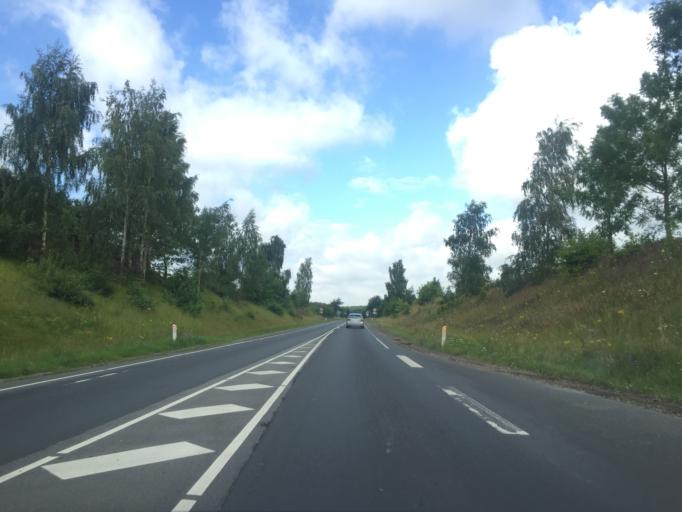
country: DK
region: South Denmark
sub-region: Svendborg Kommune
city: Svendborg
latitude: 55.0793
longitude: 10.6208
